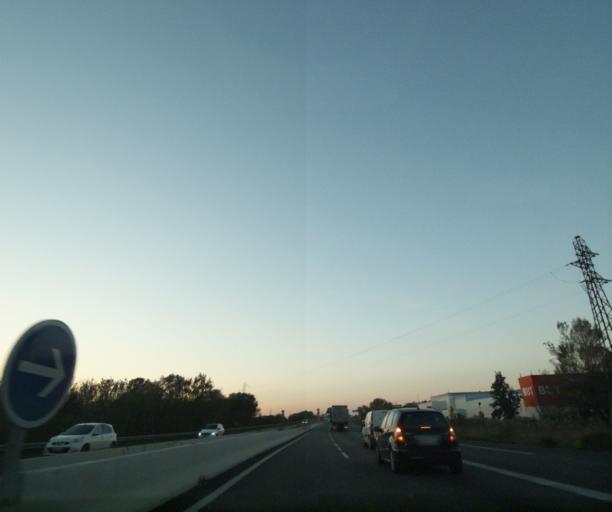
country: FR
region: Provence-Alpes-Cote d'Azur
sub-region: Departement des Bouches-du-Rhone
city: Arles
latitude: 43.6624
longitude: 4.6369
